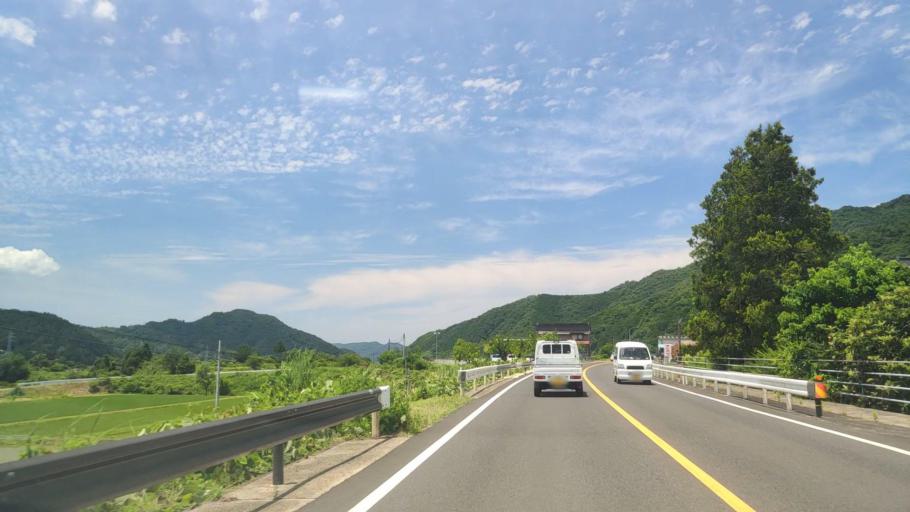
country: JP
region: Tottori
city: Tottori
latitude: 35.3704
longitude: 134.3098
